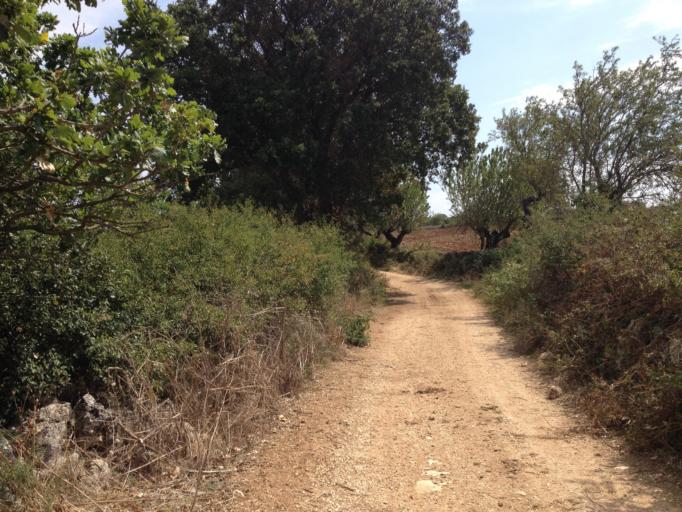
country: IT
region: Apulia
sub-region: Provincia di Bari
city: Gioia del Colle
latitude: 40.8242
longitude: 16.9747
